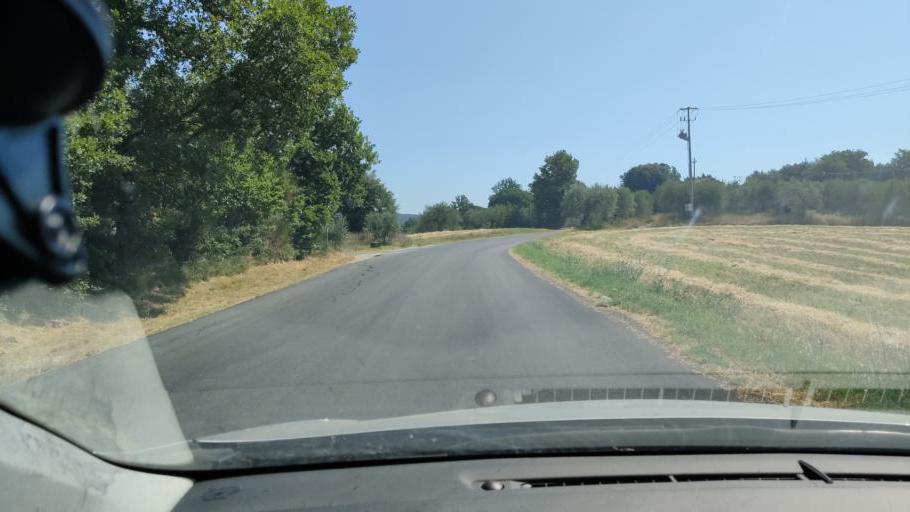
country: IT
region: Umbria
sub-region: Provincia di Terni
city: Fornole
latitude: 42.5284
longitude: 12.4434
